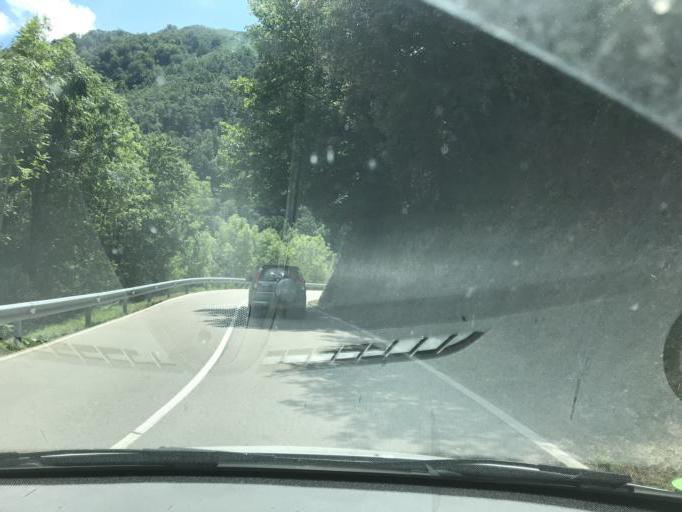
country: ES
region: Cantabria
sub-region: Provincia de Cantabria
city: Cabezon de Liebana
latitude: 43.0758
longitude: -4.5330
